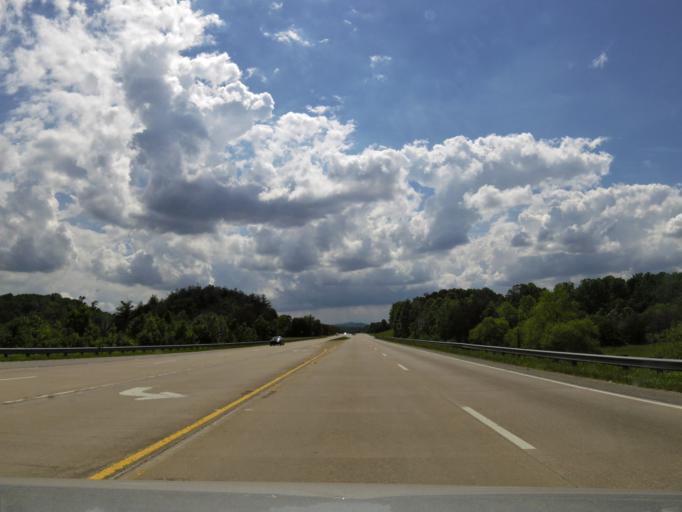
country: US
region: Georgia
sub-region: Union County
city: Blairsville
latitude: 34.8706
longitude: -83.9676
